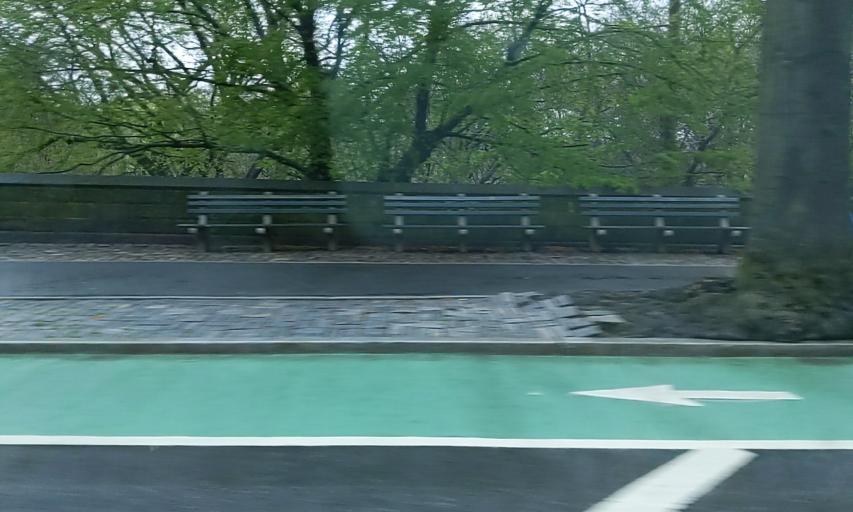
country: US
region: New York
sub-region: New York County
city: Manhattan
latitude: 40.7792
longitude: -73.9738
